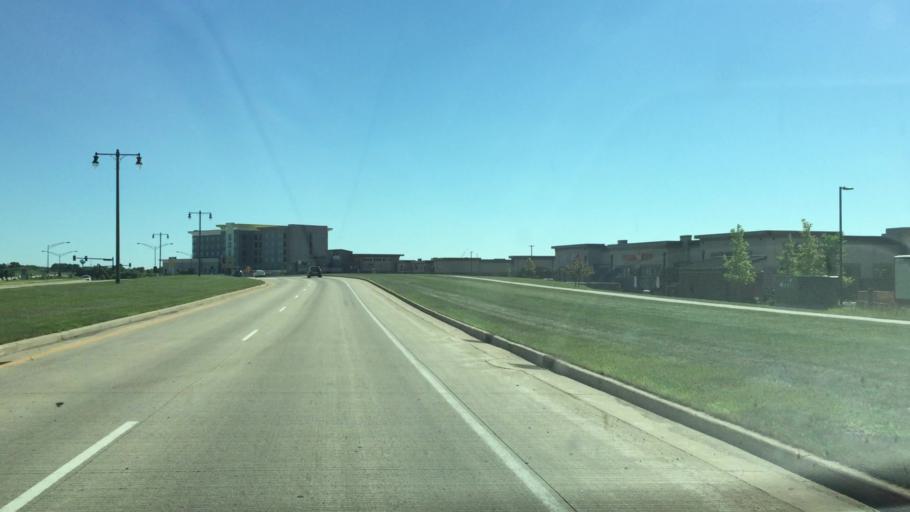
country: US
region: Wisconsin
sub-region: Dane County
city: Sun Prairie
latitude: 43.1684
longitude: -89.2676
